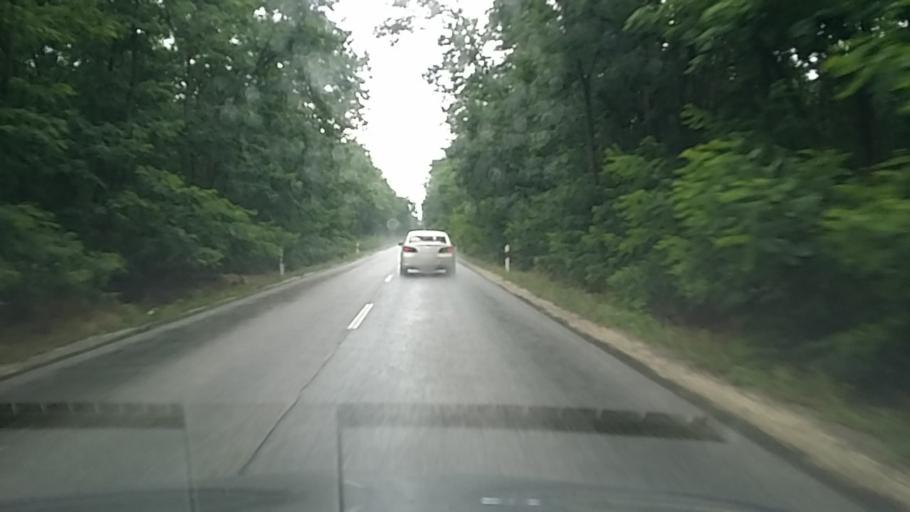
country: HU
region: Pest
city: Ullo
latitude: 47.3467
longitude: 19.3128
